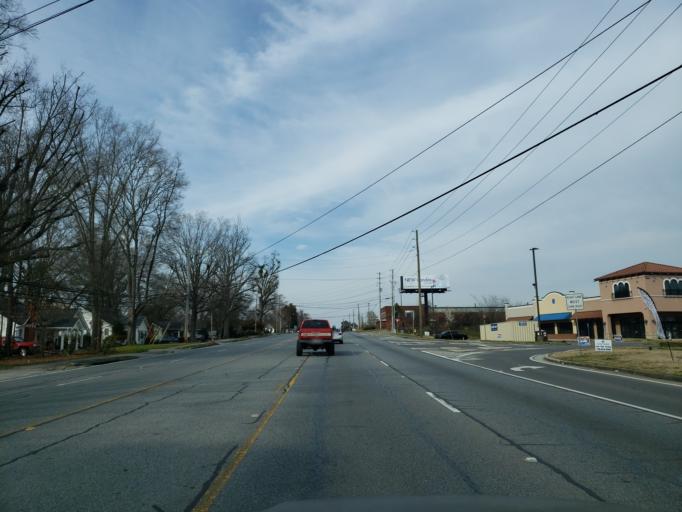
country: US
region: Georgia
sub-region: Whitfield County
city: Dalton
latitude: 34.8190
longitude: -84.9461
